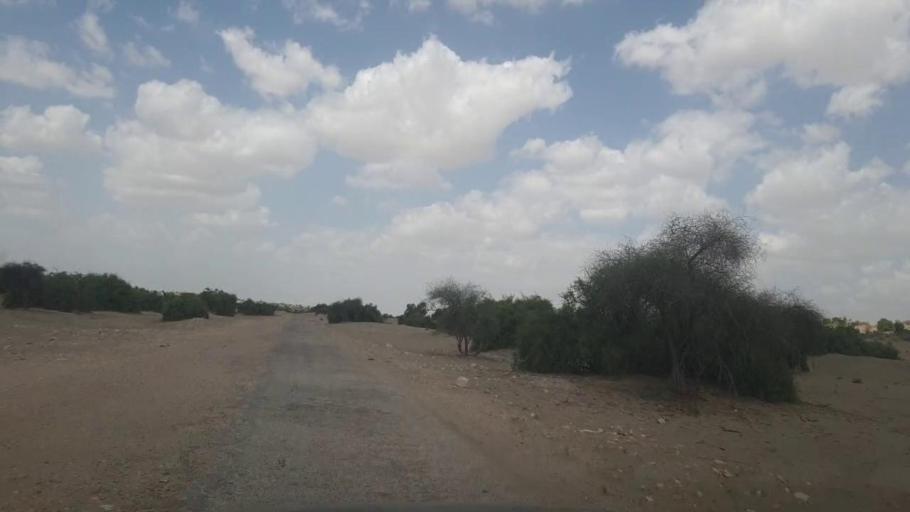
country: PK
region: Sindh
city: Kot Diji
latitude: 27.2772
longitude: 69.2216
